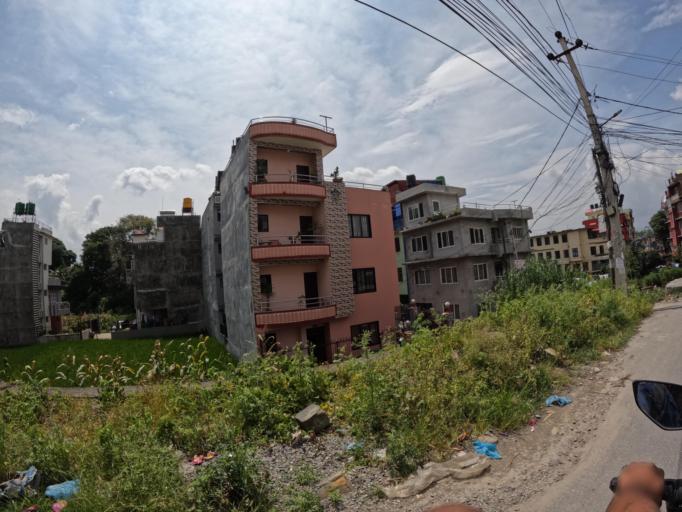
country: NP
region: Central Region
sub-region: Bagmati Zone
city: Bhaktapur
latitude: 27.6750
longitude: 85.3815
